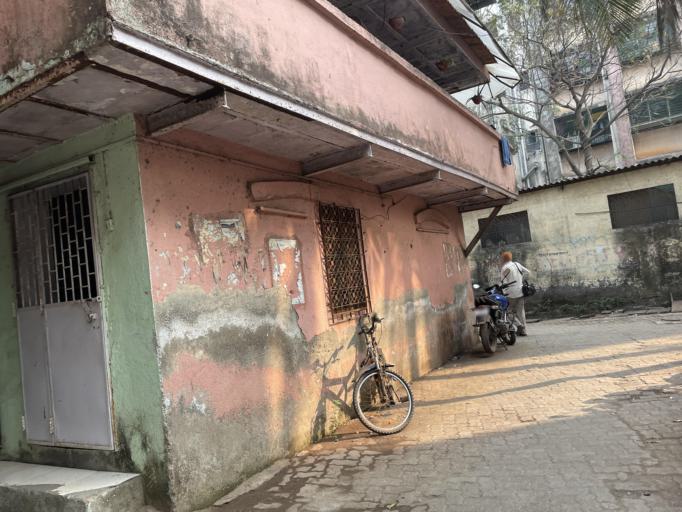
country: IN
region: Maharashtra
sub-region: Mumbai Suburban
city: Borivli
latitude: 19.1943
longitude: 72.8212
